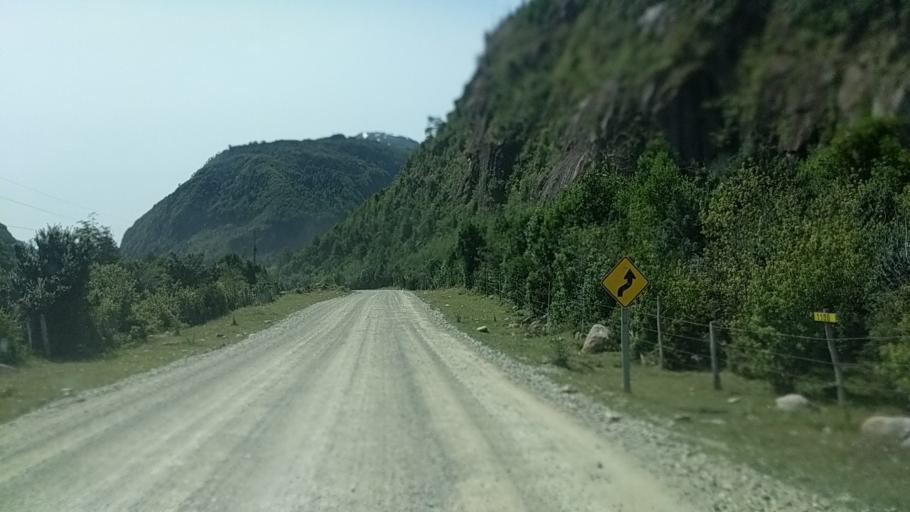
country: CL
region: Los Lagos
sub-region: Provincia de Palena
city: Palena
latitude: -43.4665
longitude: -72.1172
